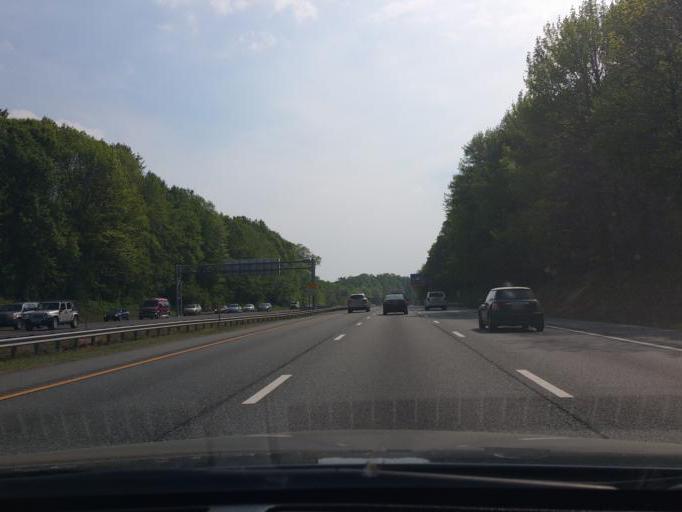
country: US
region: Maryland
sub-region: Harford County
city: Perryman
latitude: 39.5110
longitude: -76.2092
